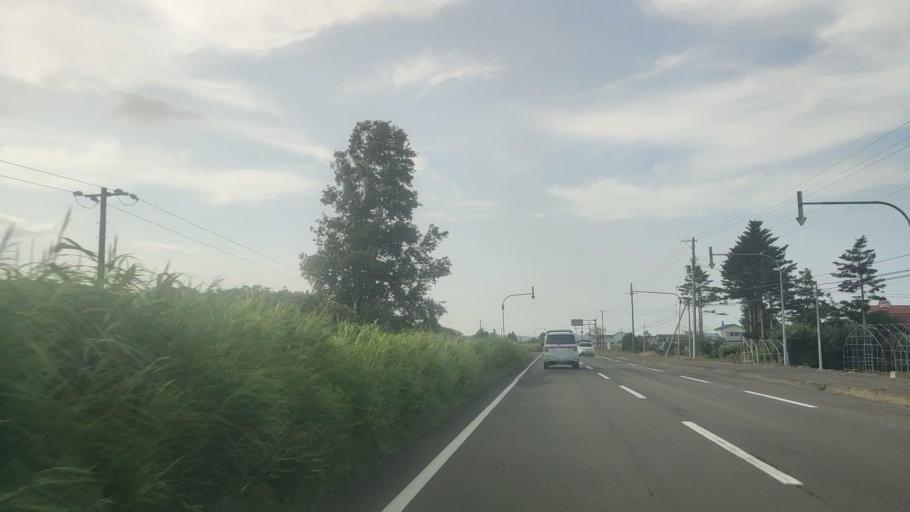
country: JP
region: Hokkaido
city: Iwamizawa
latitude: 42.9898
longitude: 141.7913
